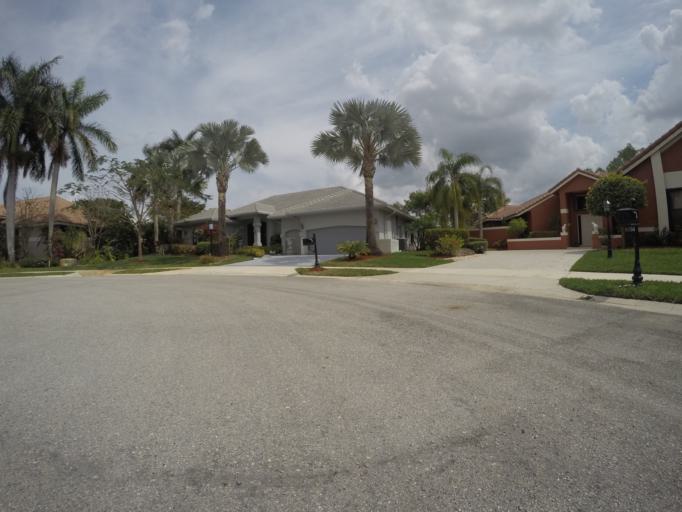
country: US
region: Florida
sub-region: Palm Beach County
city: Villages of Oriole
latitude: 26.4099
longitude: -80.2160
